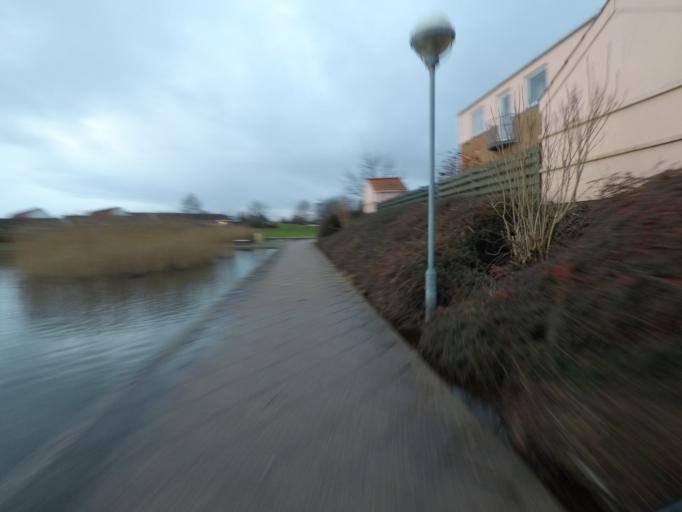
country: DK
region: Capital Region
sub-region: Ballerup Kommune
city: Ballerup
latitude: 55.7502
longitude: 12.3763
